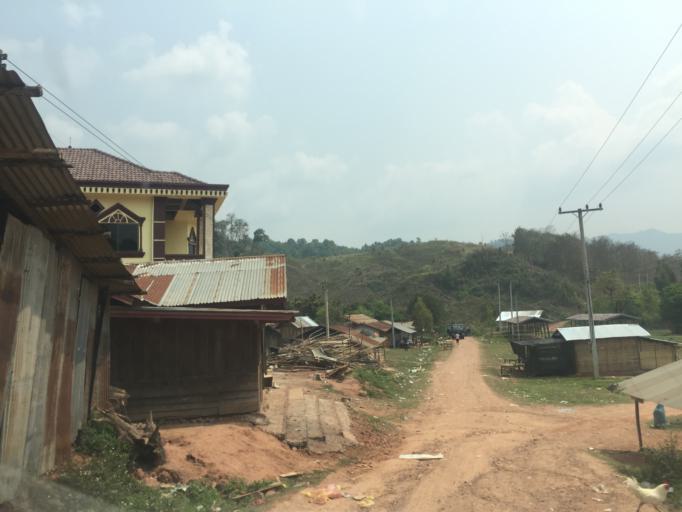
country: LA
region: Loungnamtha
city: Muang Nale
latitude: 20.2011
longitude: 101.6648
